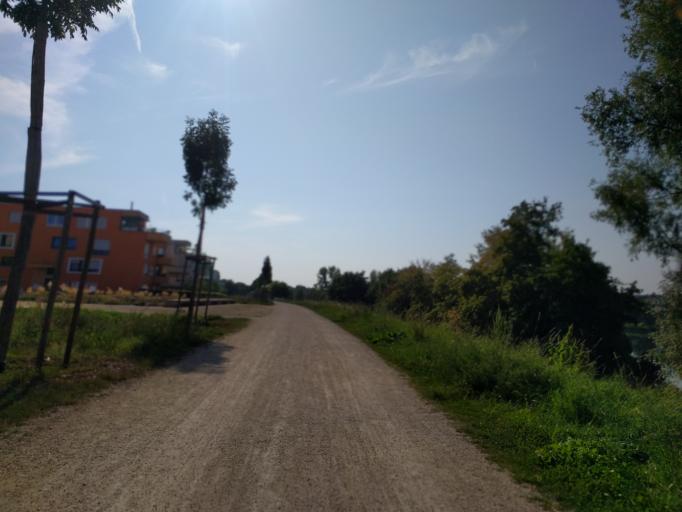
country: DE
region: Bavaria
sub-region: Upper Palatinate
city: Regensburg
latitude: 49.0249
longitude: 12.1067
